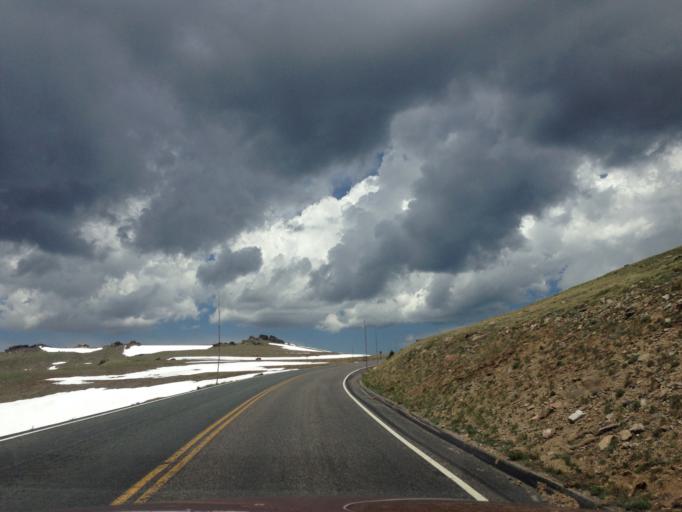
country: US
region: Colorado
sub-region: Larimer County
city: Estes Park
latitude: 40.4062
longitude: -105.7161
